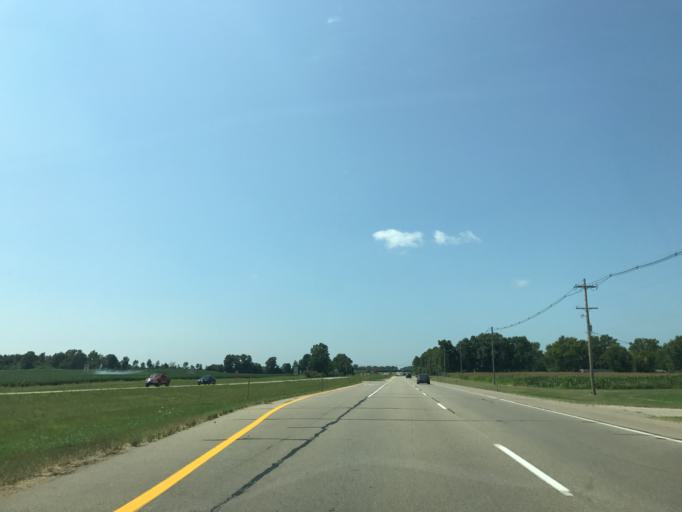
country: US
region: Michigan
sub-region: Berrien County
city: Niles
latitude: 41.8053
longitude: -86.3042
